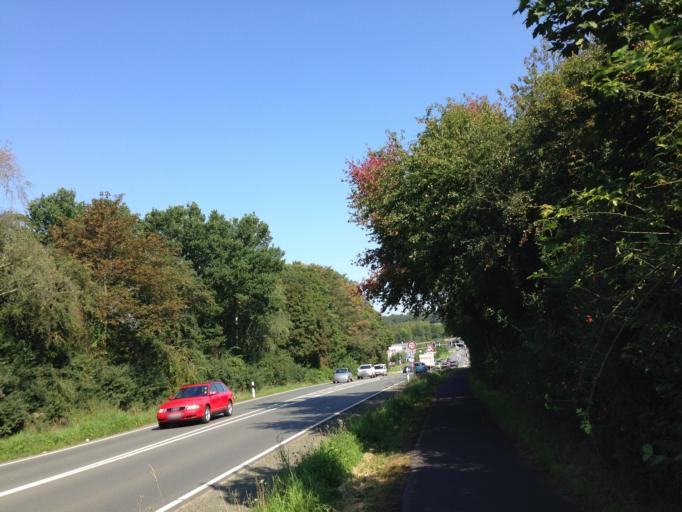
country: DE
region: Hesse
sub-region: Regierungsbezirk Giessen
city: Hoernsheim
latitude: 50.5358
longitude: 8.6498
